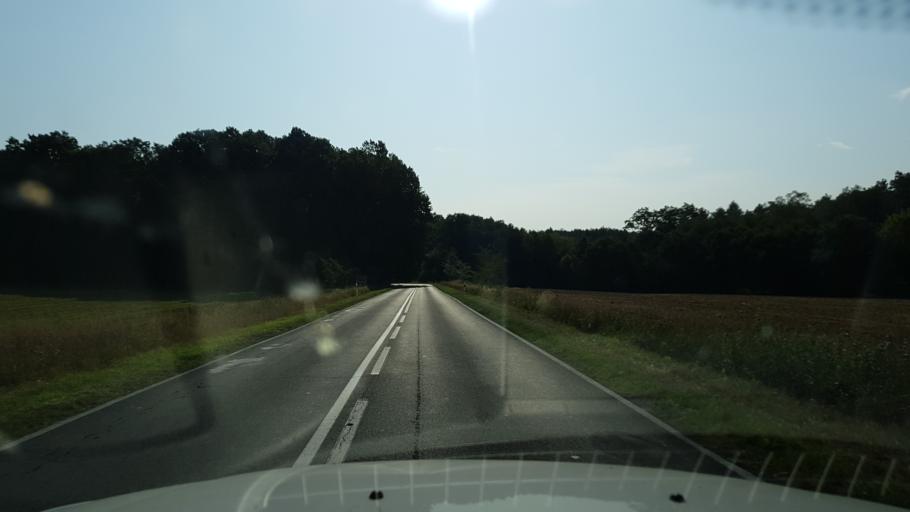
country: PL
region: West Pomeranian Voivodeship
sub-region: Powiat lobeski
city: Resko
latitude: 53.7728
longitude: 15.4424
